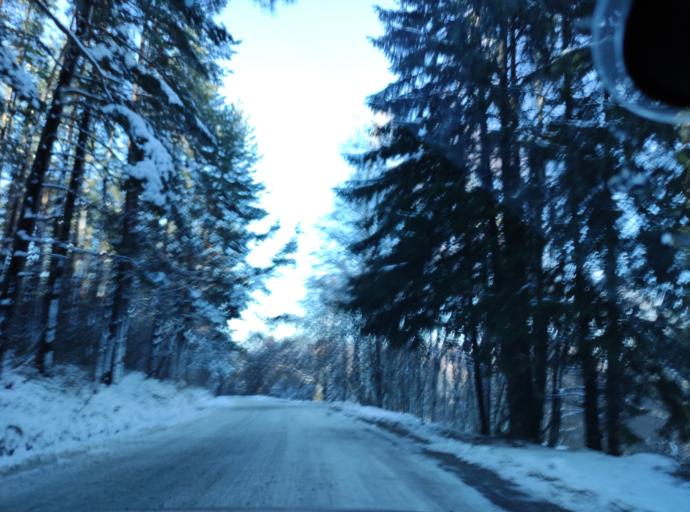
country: BG
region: Sofia-Capital
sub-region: Stolichna Obshtina
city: Sofia
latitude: 42.6023
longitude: 23.3026
